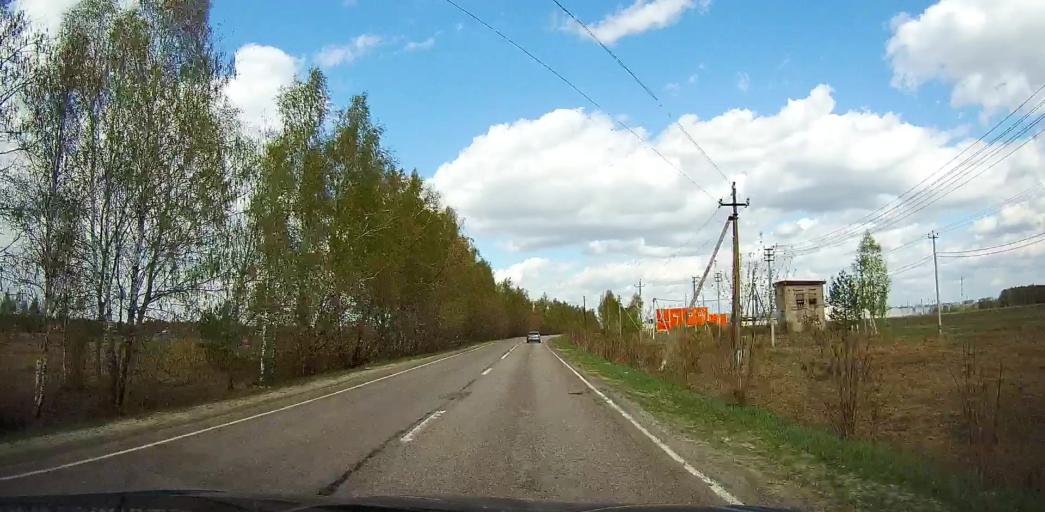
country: RU
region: Moskovskaya
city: Davydovo
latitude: 55.6001
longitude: 38.8416
